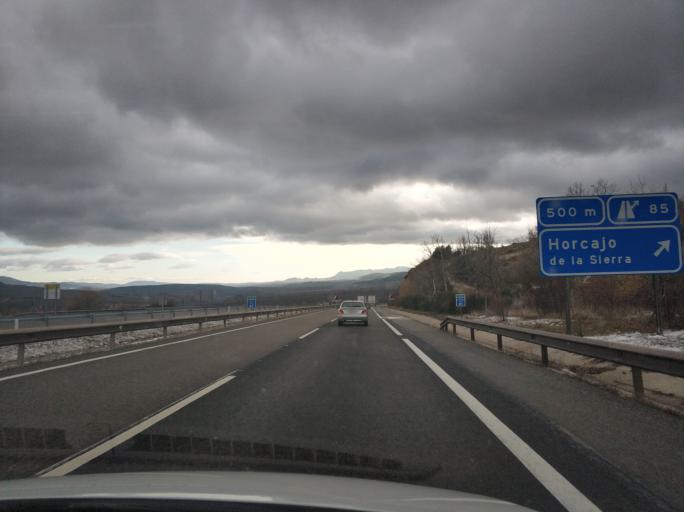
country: ES
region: Madrid
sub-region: Provincia de Madrid
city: Robregordo
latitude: 41.0894
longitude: -3.5956
